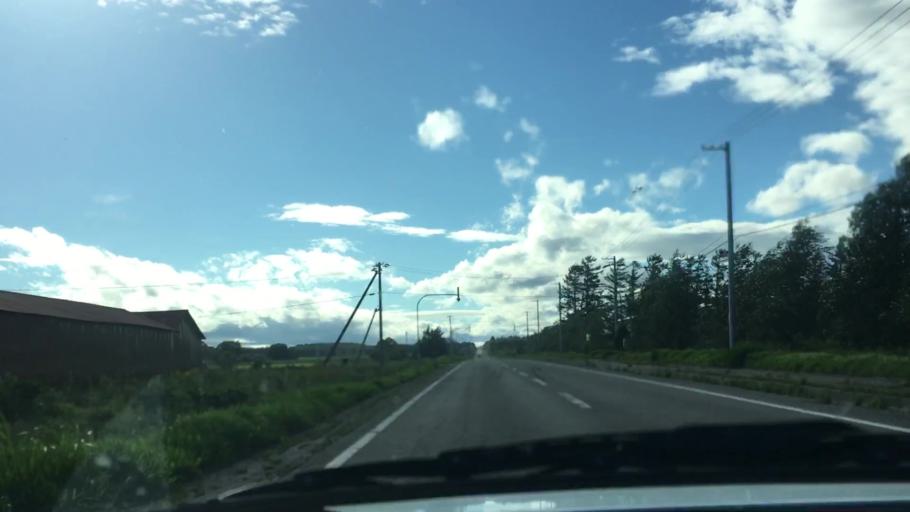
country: JP
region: Hokkaido
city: Otofuke
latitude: 43.1590
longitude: 143.1714
